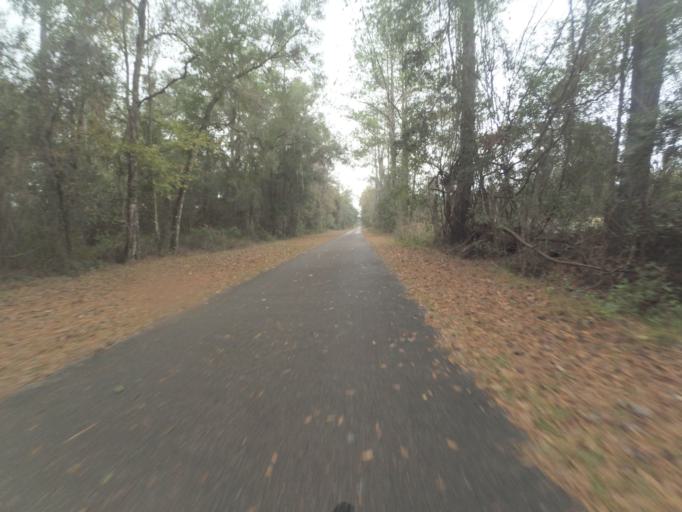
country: US
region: Florida
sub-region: Alachua County
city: Hawthorne
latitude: 29.5947
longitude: -82.2087
